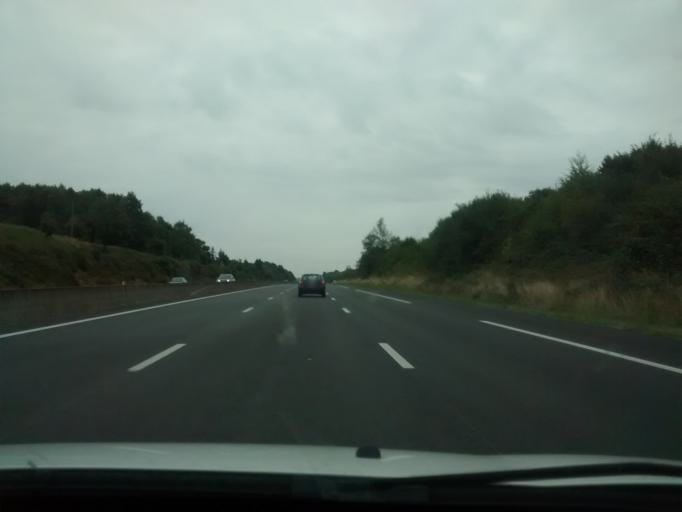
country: FR
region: Pays de la Loire
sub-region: Departement de la Sarthe
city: Tuffe
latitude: 48.0912
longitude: 0.5137
